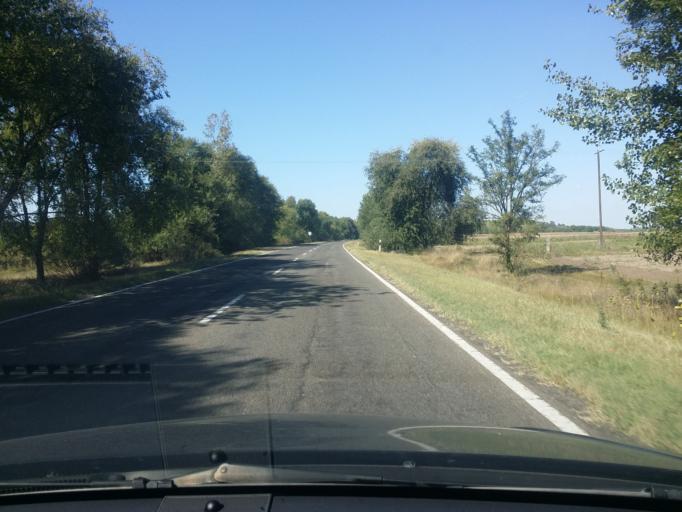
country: HU
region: Bacs-Kiskun
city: Palmonostora
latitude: 46.6159
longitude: 19.9063
